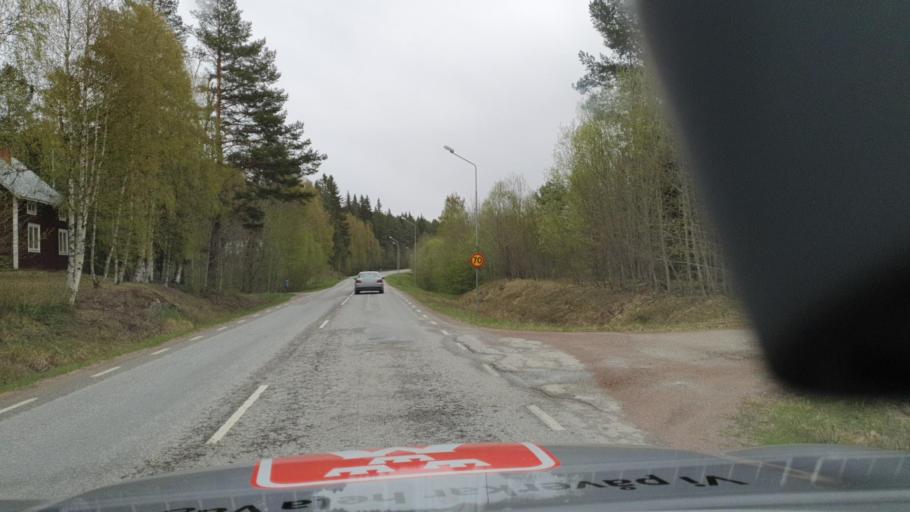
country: SE
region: Vaesternorrland
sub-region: Solleftea Kommun
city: As
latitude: 63.6893
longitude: 16.9152
